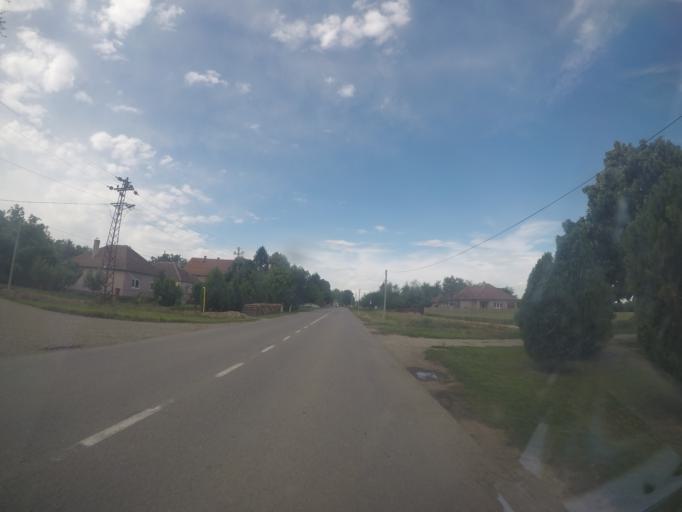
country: RS
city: Perlez
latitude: 45.2153
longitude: 20.3869
